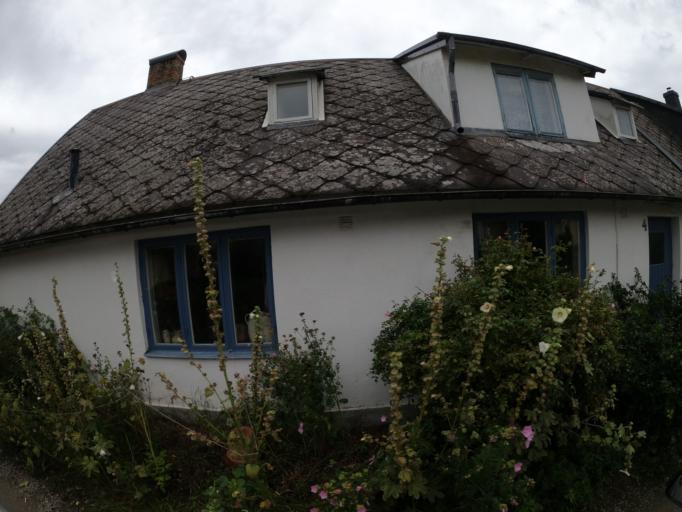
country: SE
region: Skane
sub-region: Lunds Kommun
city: Lund
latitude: 55.7767
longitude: 13.2294
